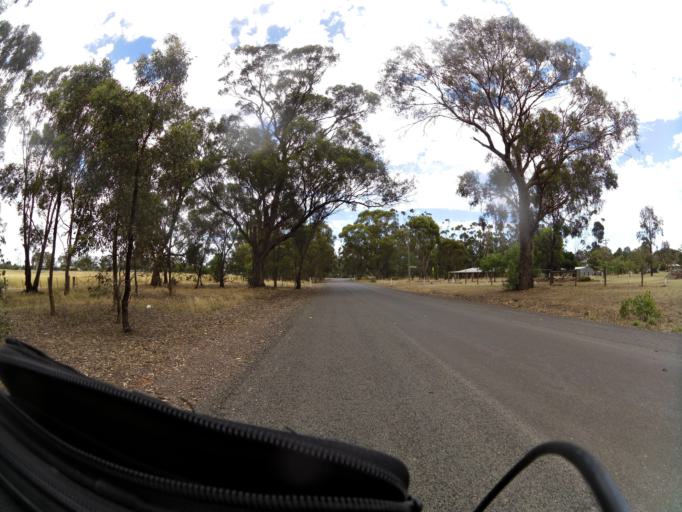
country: AU
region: Victoria
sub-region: Campaspe
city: Kyabram
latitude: -36.7403
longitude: 145.1368
